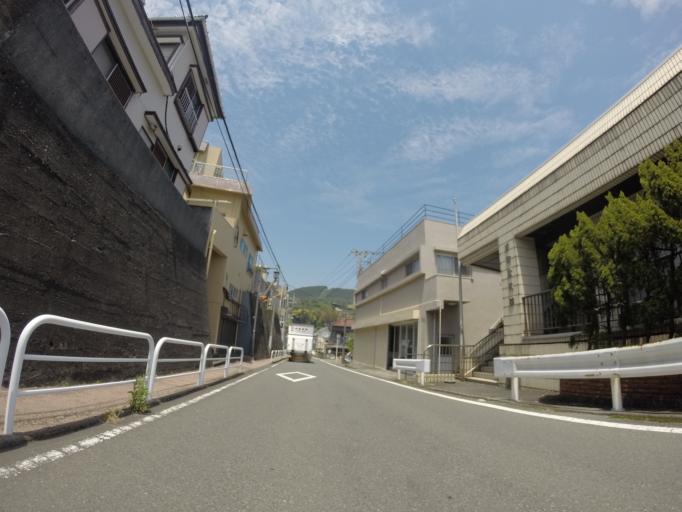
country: JP
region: Shizuoka
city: Shimoda
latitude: 34.7725
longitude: 139.0407
